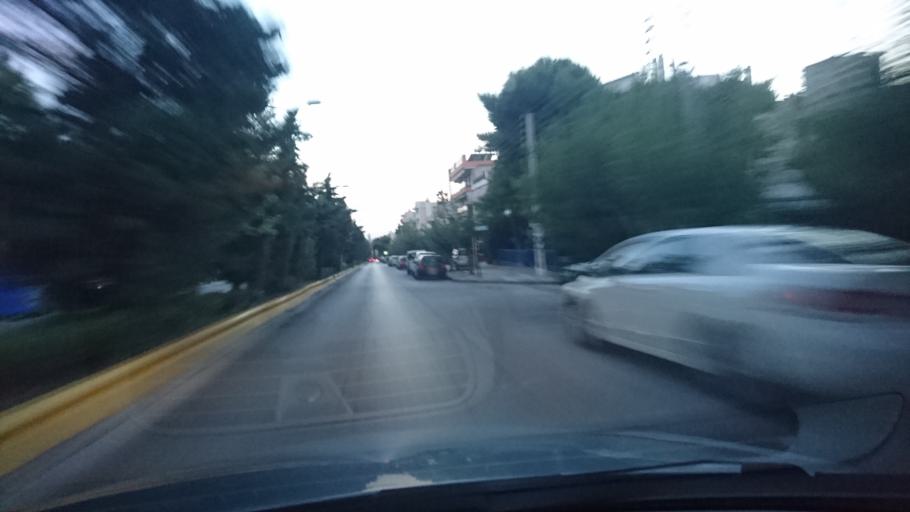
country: GR
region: Attica
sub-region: Nomarchia Athinas
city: Ilioupoli
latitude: 37.9272
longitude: 23.7531
